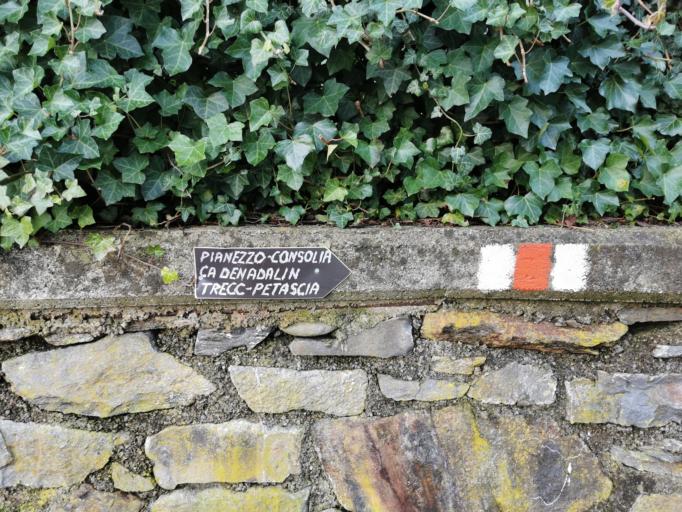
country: IT
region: Lombardy
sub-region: Provincia di Sondrio
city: Regoledo
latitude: 46.1286
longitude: 9.5489
